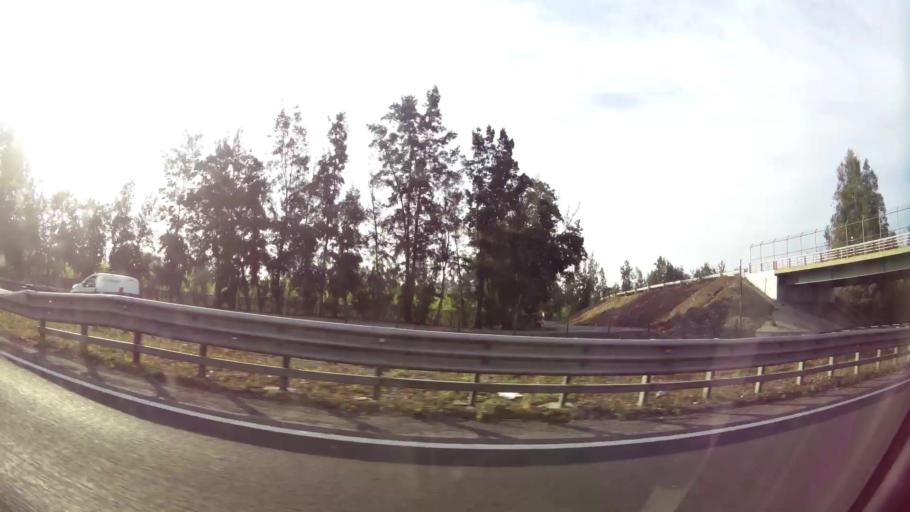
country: CL
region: Santiago Metropolitan
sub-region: Provincia de Talagante
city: Penaflor
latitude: -33.6227
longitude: -70.8606
